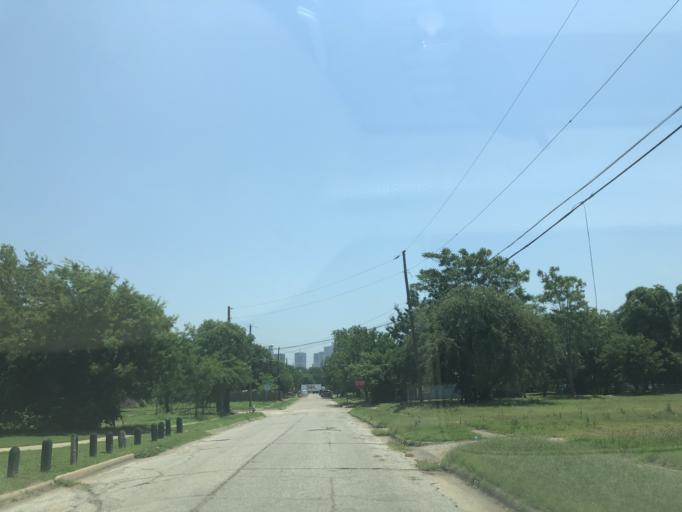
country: US
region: Texas
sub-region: Dallas County
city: Dallas
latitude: 32.7821
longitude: -96.8384
